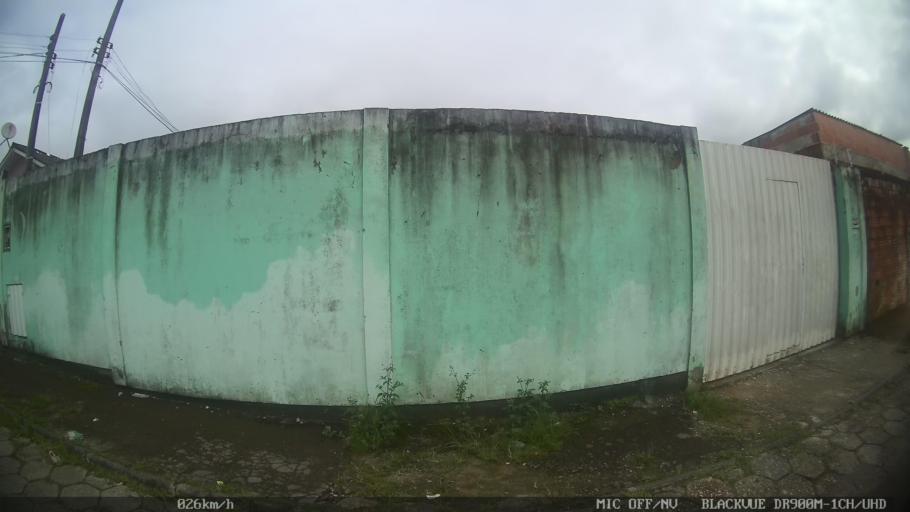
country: BR
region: Santa Catarina
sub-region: Biguacu
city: Biguacu
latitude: -27.5486
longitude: -48.6448
